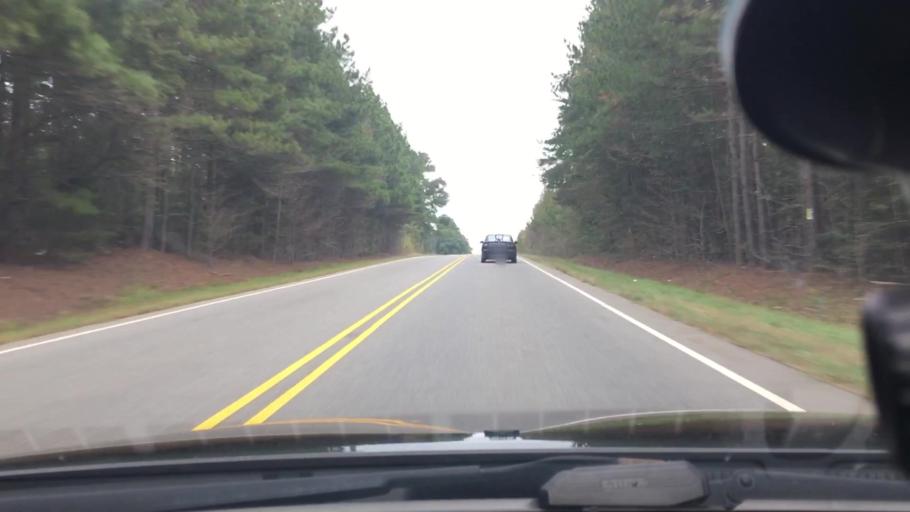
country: US
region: North Carolina
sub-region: Montgomery County
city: Biscoe
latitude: 35.3603
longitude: -79.7115
